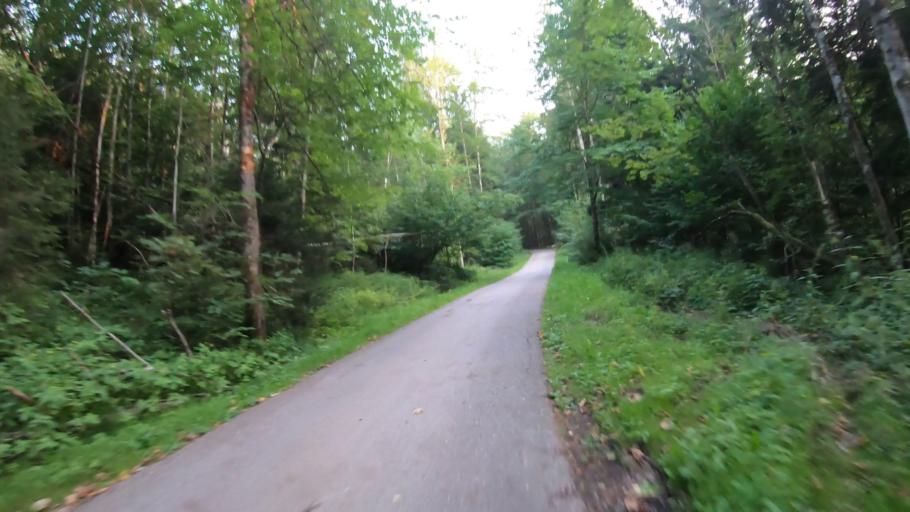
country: DE
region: Bavaria
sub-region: Upper Bavaria
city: Ruhpolding
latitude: 47.7794
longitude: 12.6578
